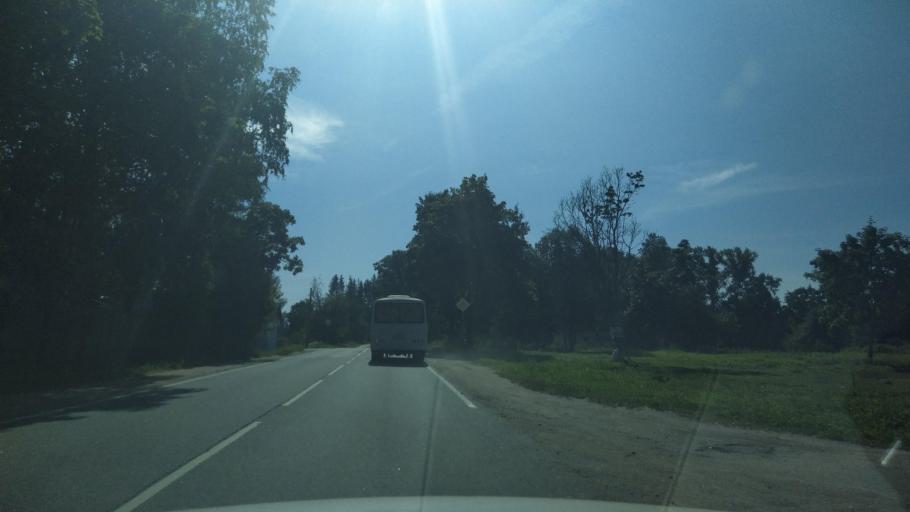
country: RU
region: Leningrad
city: Siverskiy
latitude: 59.3175
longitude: 30.0711
